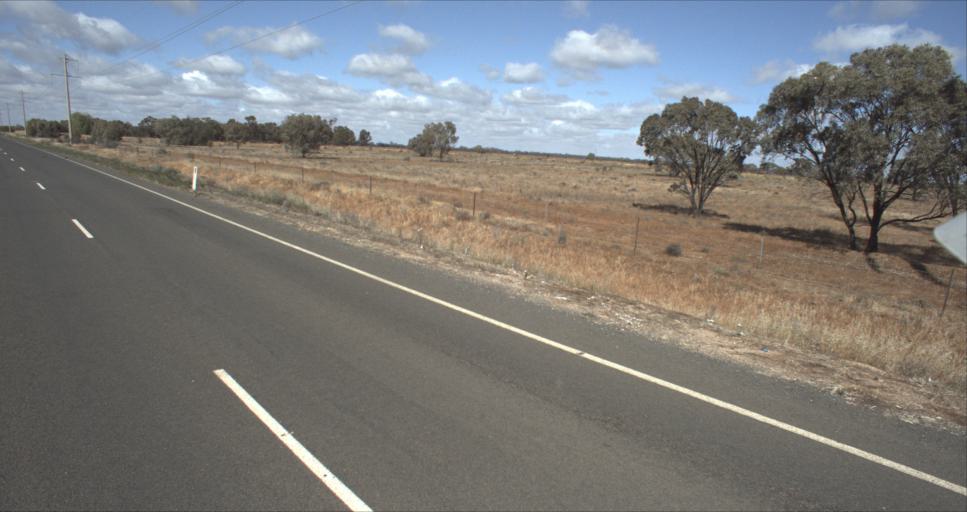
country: AU
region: New South Wales
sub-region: Murrumbidgee Shire
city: Darlington Point
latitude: -34.5257
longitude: 146.1749
